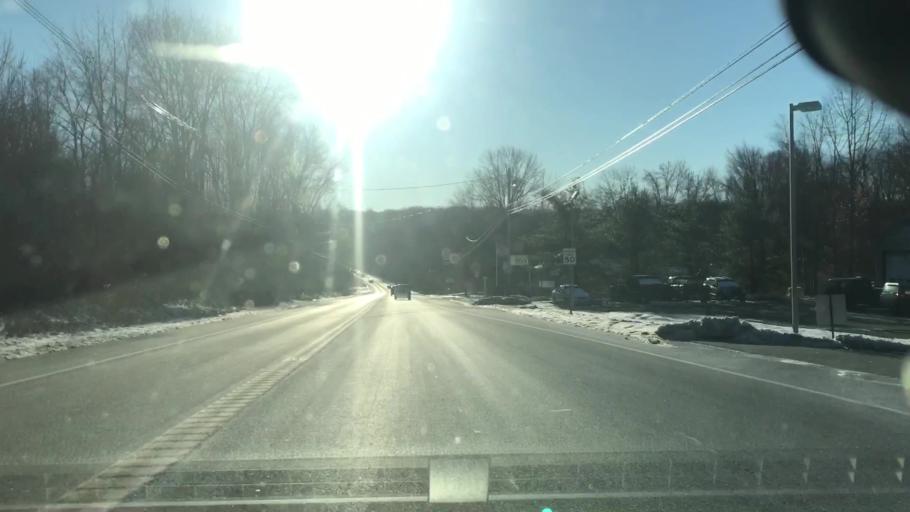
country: US
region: New Jersey
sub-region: Morris County
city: Chester
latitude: 40.8015
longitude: -74.7128
